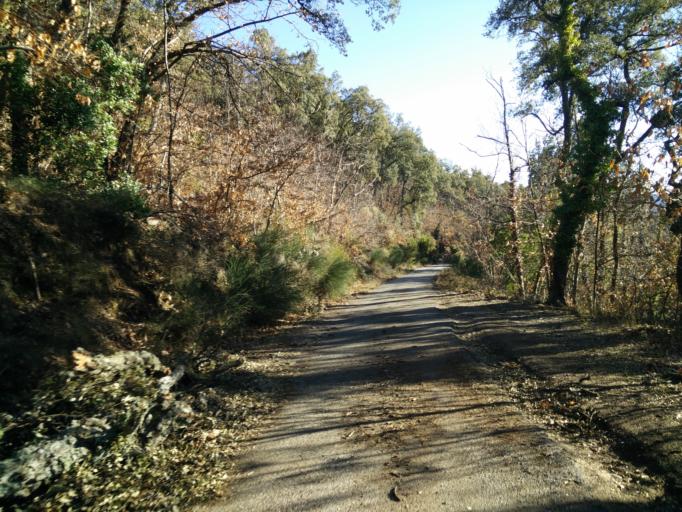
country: FR
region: Provence-Alpes-Cote d'Azur
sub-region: Departement du Var
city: Collobrieres
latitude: 43.2776
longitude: 6.2962
